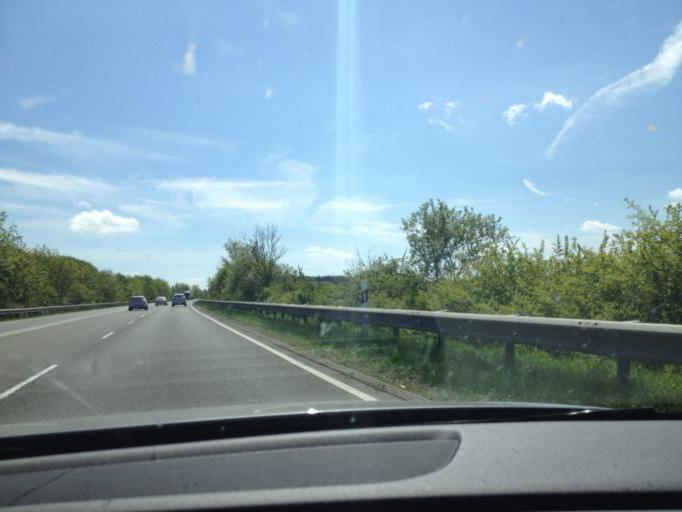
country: DE
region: North Rhine-Westphalia
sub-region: Regierungsbezirk Koln
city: Blankenheim
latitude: 50.4359
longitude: 6.6103
